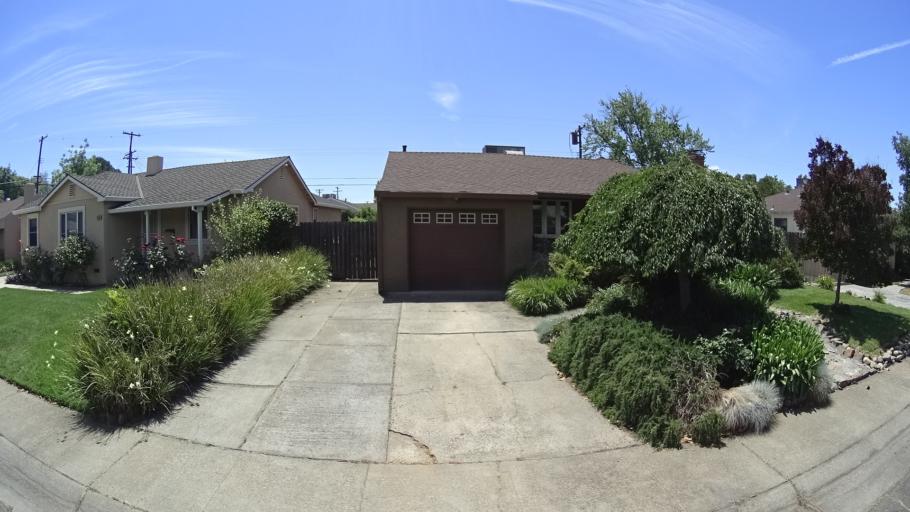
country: US
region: California
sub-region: Sacramento County
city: Parkway
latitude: 38.5215
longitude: -121.4376
